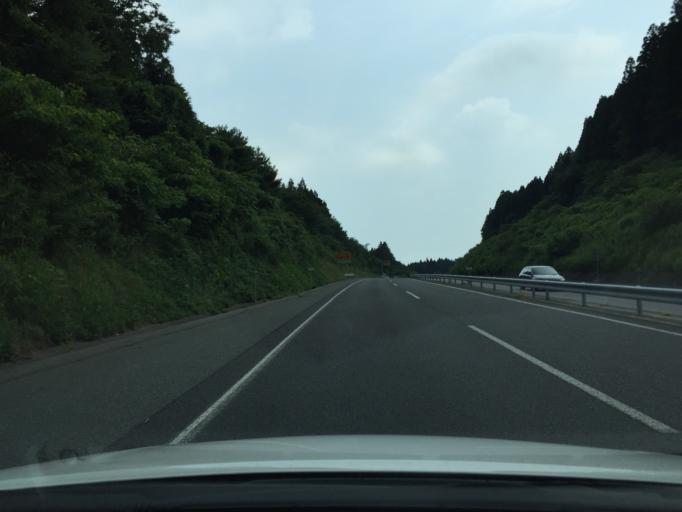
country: JP
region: Fukushima
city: Iwaki
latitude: 37.0944
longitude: 140.7829
